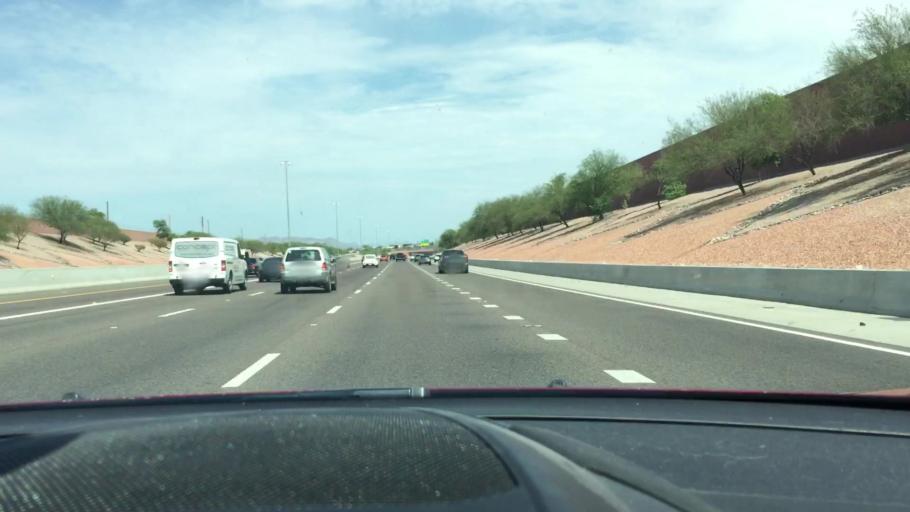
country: US
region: Arizona
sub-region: Maricopa County
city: Mesa
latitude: 33.4656
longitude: -111.8023
